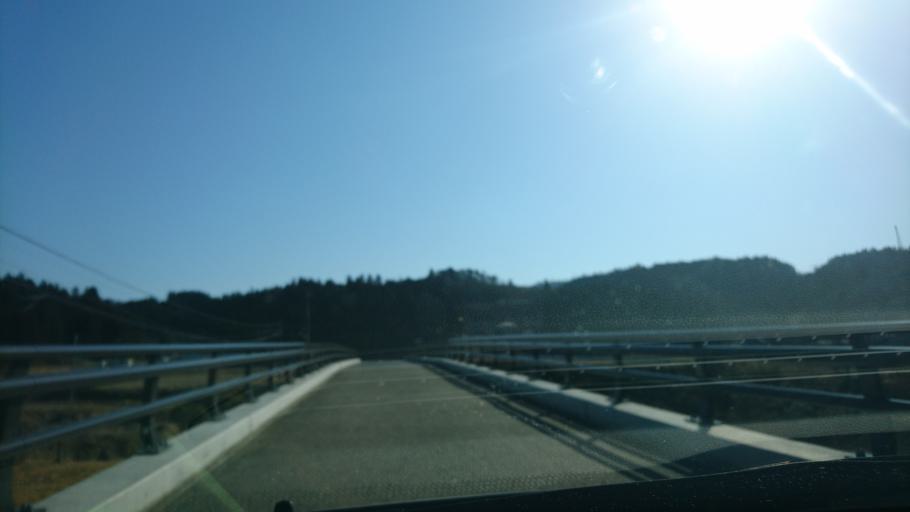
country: JP
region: Iwate
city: Ichinoseki
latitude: 38.8481
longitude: 141.2947
